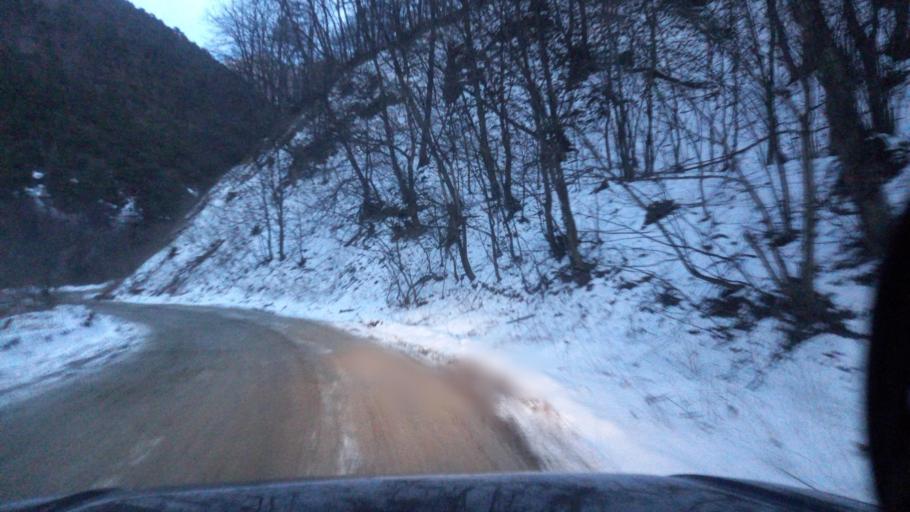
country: RU
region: Ingushetiya
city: Dzhayrakh
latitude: 42.8261
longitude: 44.6020
